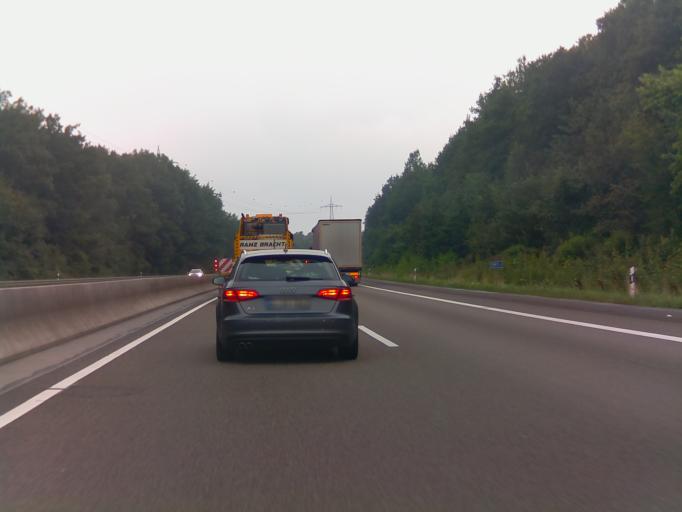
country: DE
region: Hesse
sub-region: Regierungsbezirk Kassel
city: Petersberg
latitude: 50.5926
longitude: 9.6885
